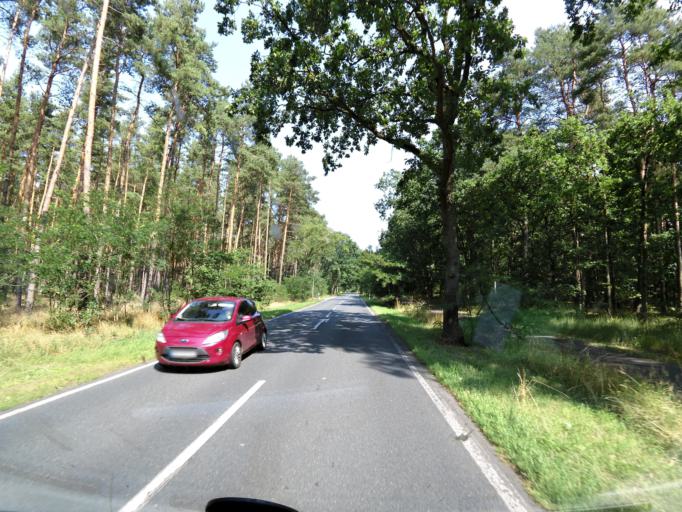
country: DE
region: Brandenburg
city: Liebenwalde
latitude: 52.8421
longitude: 13.3225
